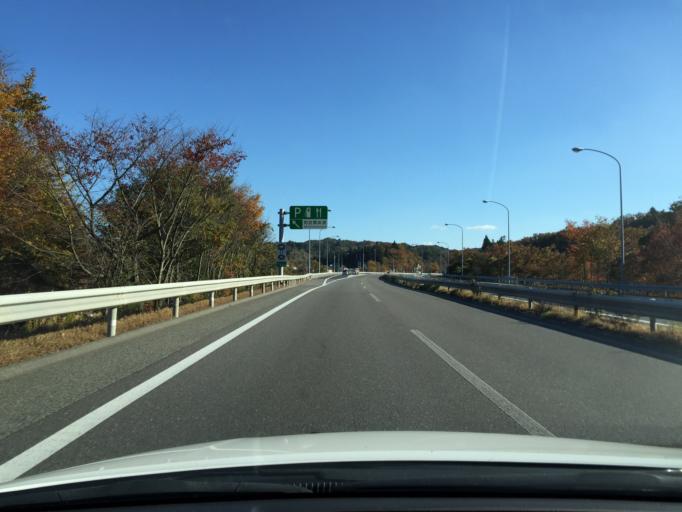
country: JP
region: Fukushima
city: Funehikimachi-funehiki
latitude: 37.3901
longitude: 140.5927
